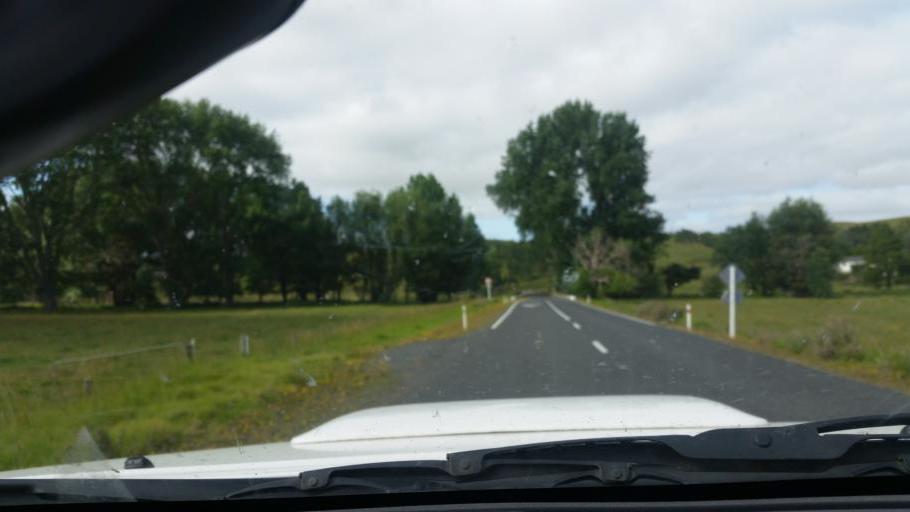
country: NZ
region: Northland
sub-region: Kaipara District
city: Dargaville
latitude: -35.8403
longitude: 173.8442
